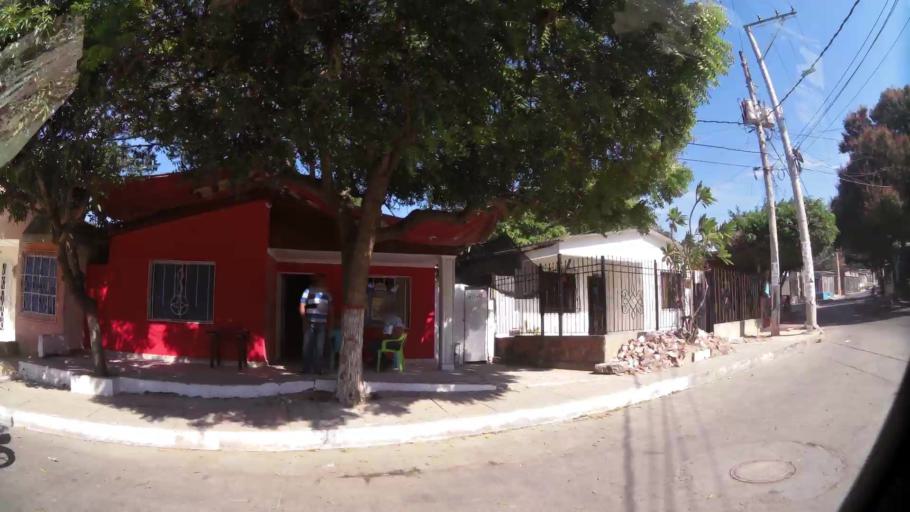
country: CO
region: Atlantico
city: Barranquilla
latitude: 10.9287
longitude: -74.8176
